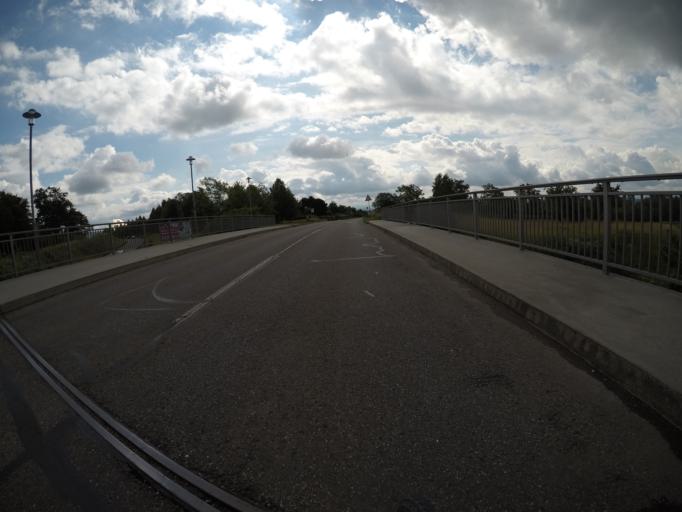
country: DE
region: Baden-Wuerttemberg
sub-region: Regierungsbezirk Stuttgart
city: Ostfildern
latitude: 48.7242
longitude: 9.2741
